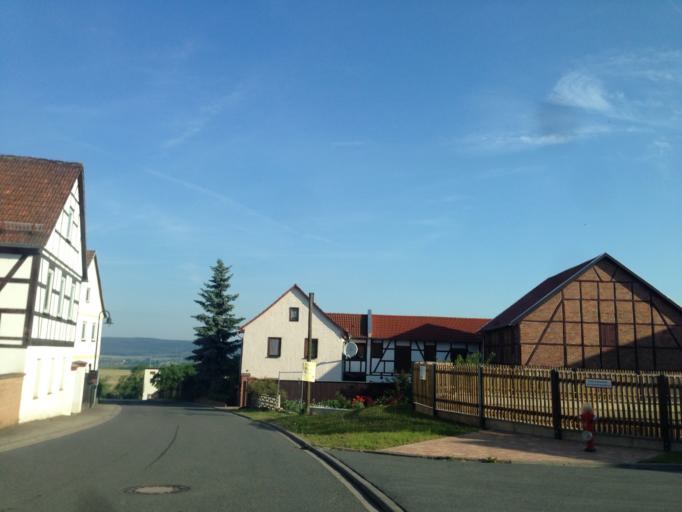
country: DE
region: Thuringia
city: Seisla
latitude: 50.6507
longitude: 11.5347
